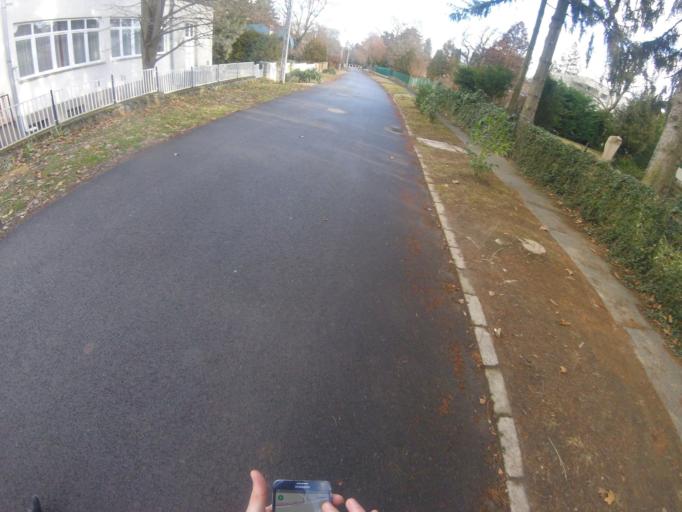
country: HU
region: Somogy
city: Balatonfoldvar
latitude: 46.8469
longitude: 17.8697
